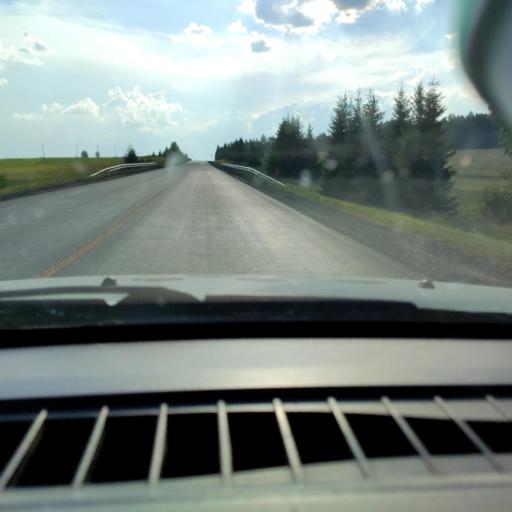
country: RU
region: Udmurtiya
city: Debesy
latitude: 57.6997
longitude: 54.0399
